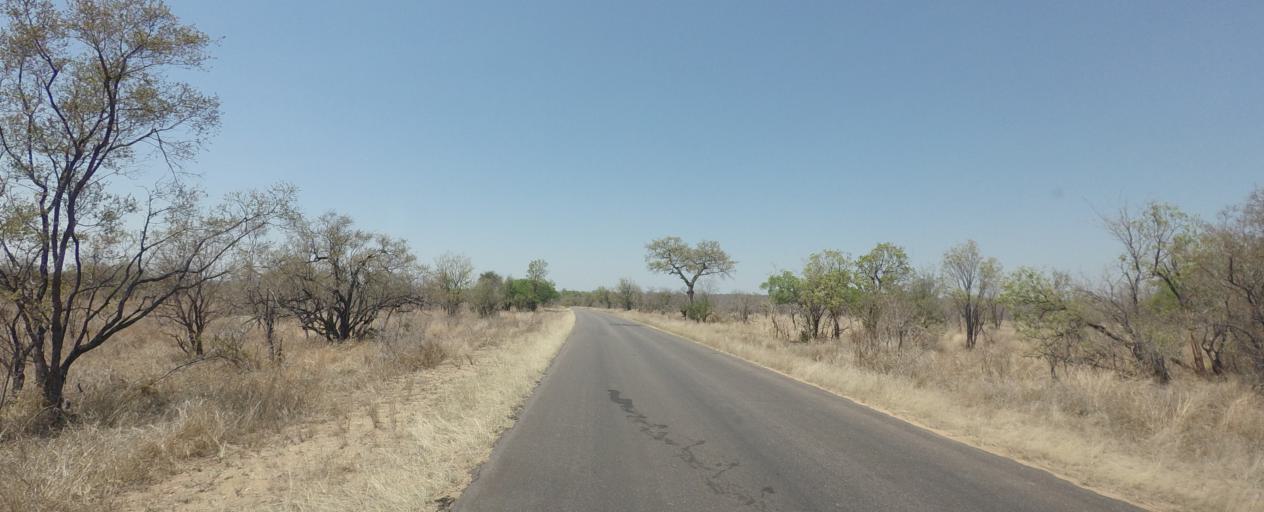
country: ZA
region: Limpopo
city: Thulamahashi
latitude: -24.4727
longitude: 31.4245
